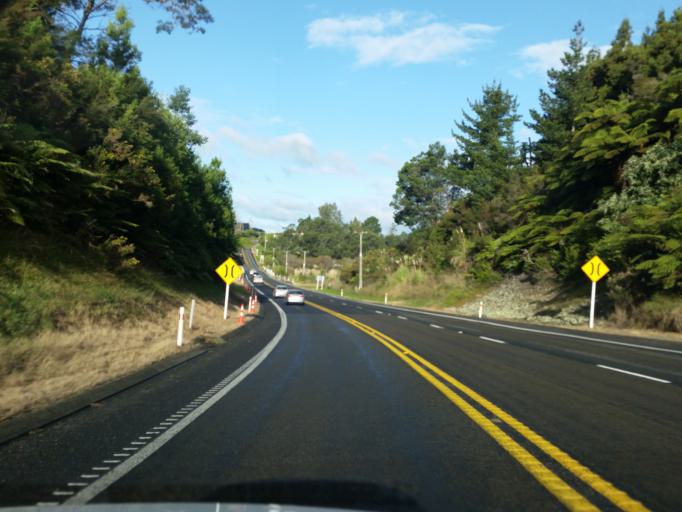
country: NZ
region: Bay of Plenty
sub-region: Western Bay of Plenty District
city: Katikati
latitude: -37.6330
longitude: 175.9578
